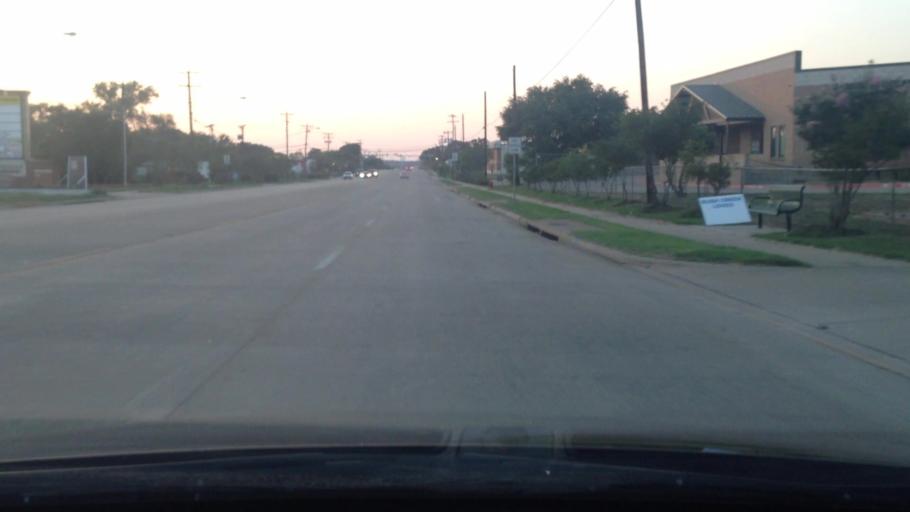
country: US
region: Texas
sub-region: Tarrant County
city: Kennedale
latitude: 32.6485
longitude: -97.2233
